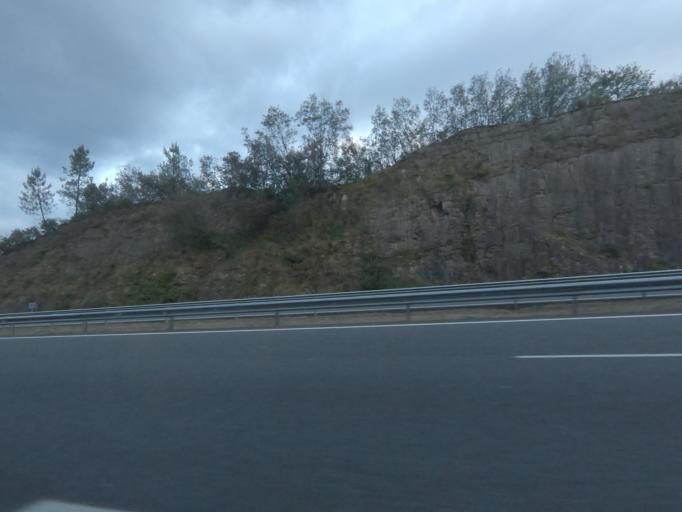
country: ES
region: Galicia
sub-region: Provincia de Ourense
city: Carballeda de Avia
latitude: 42.3060
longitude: -8.1536
